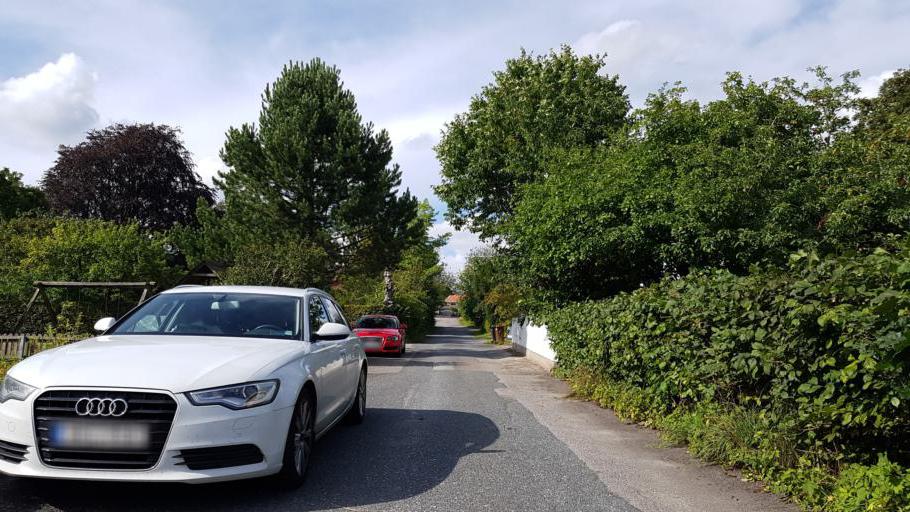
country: SE
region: Vaestra Goetaland
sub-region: Harryda Kommun
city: Molnlycke
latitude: 57.6622
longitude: 12.1183
